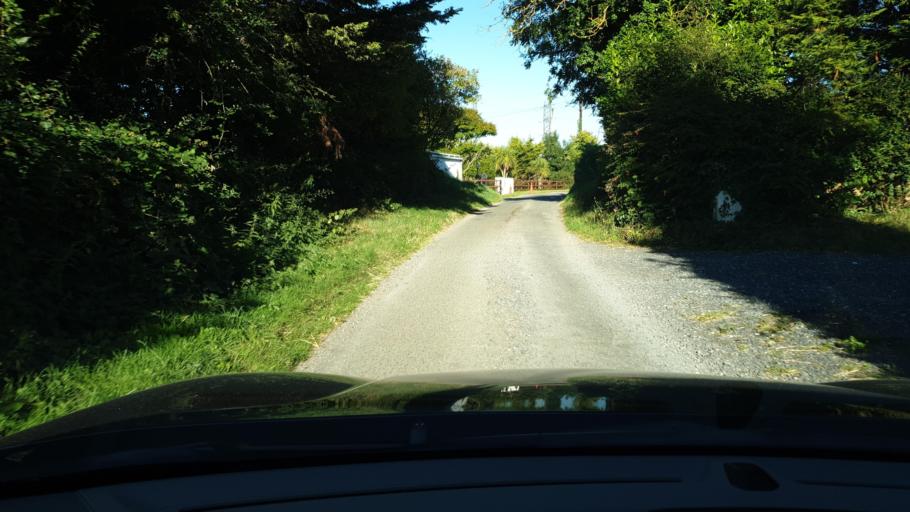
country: IE
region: Leinster
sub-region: Fingal County
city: Blanchardstown
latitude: 53.4374
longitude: -6.3608
